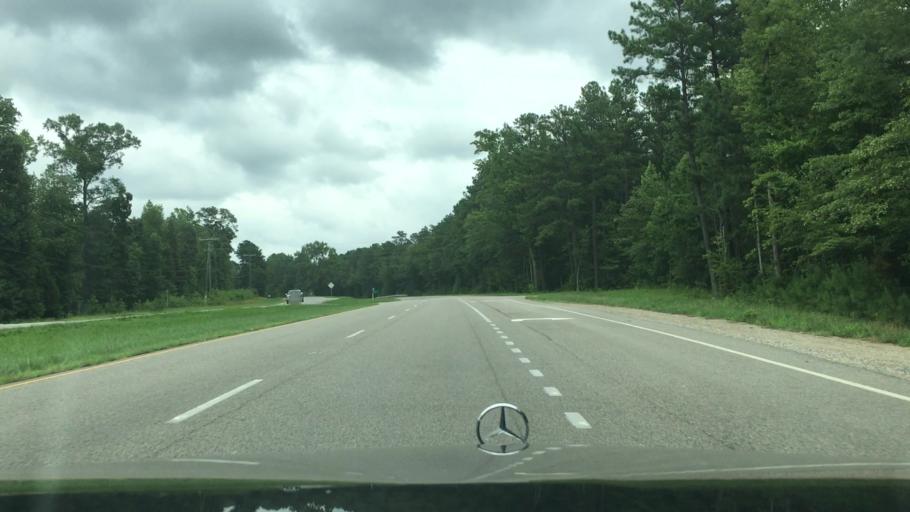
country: US
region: Virginia
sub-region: Chesterfield County
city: Woodlake
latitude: 37.3930
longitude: -77.7898
